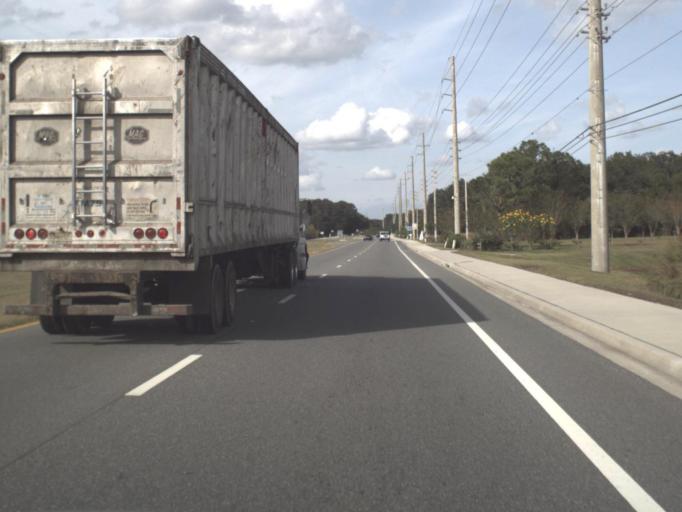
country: US
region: Florida
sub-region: Osceola County
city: Saint Cloud
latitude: 28.3355
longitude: -81.2281
